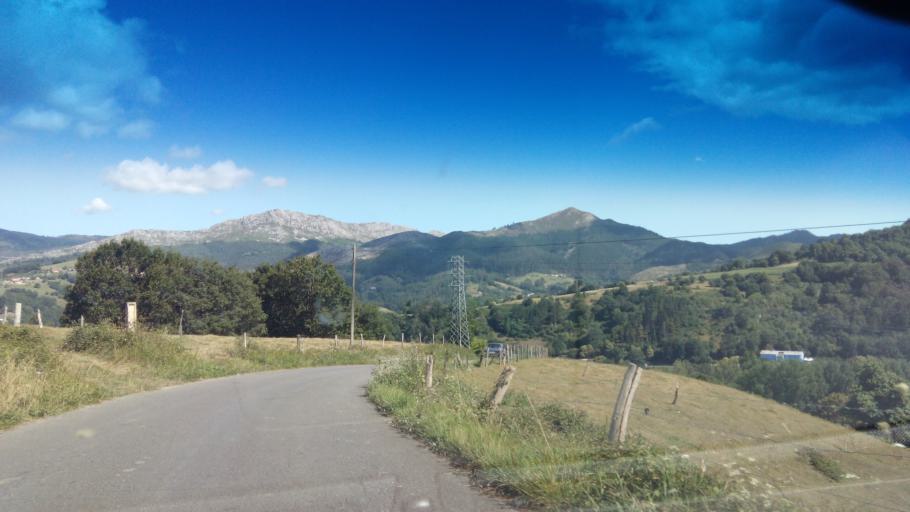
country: ES
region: Asturias
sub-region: Province of Asturias
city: Parres
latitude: 43.3782
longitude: -5.1773
